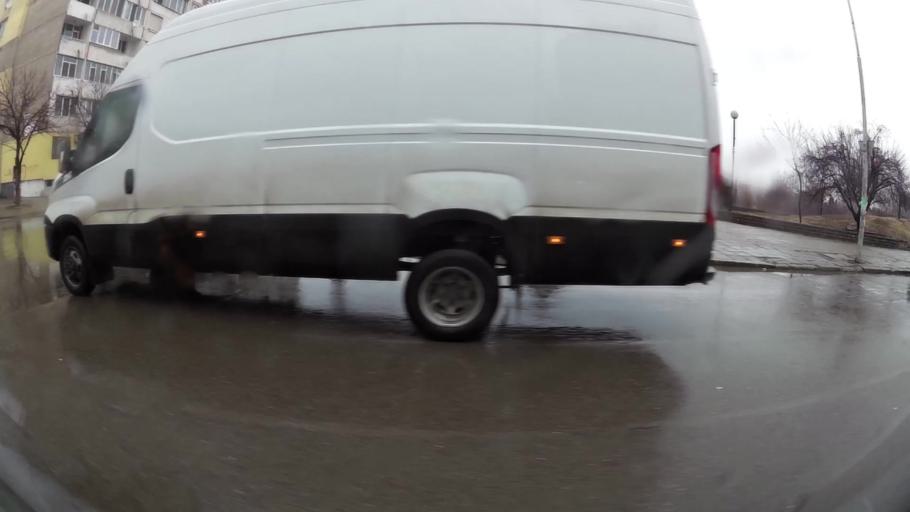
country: BG
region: Sofia-Capital
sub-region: Stolichna Obshtina
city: Sofia
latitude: 42.6622
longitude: 23.3974
